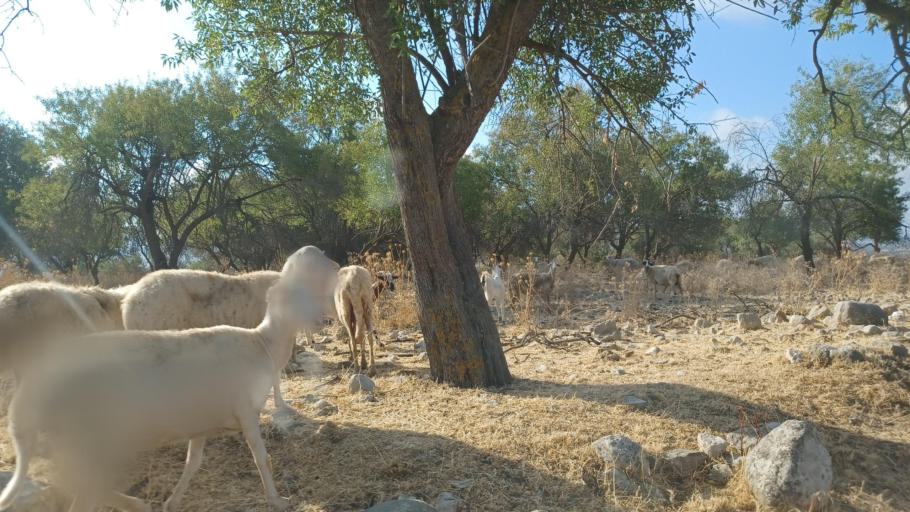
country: CY
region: Pafos
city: Mesogi
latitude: 34.8584
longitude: 32.5885
